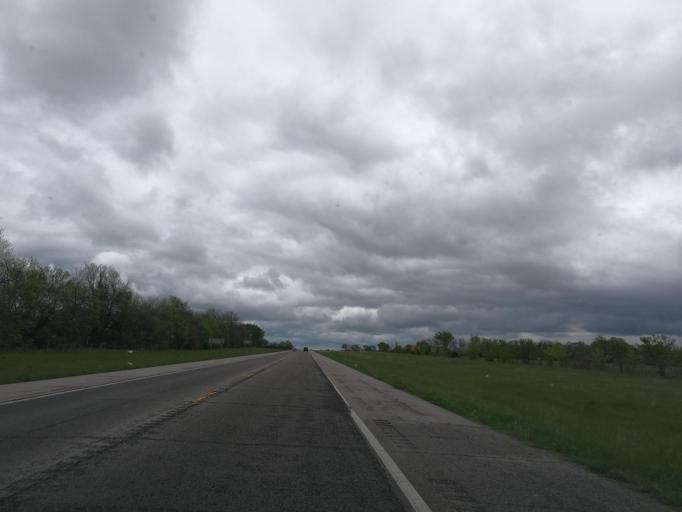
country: US
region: Kansas
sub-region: Labette County
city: Parsons
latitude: 37.3429
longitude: -95.4102
